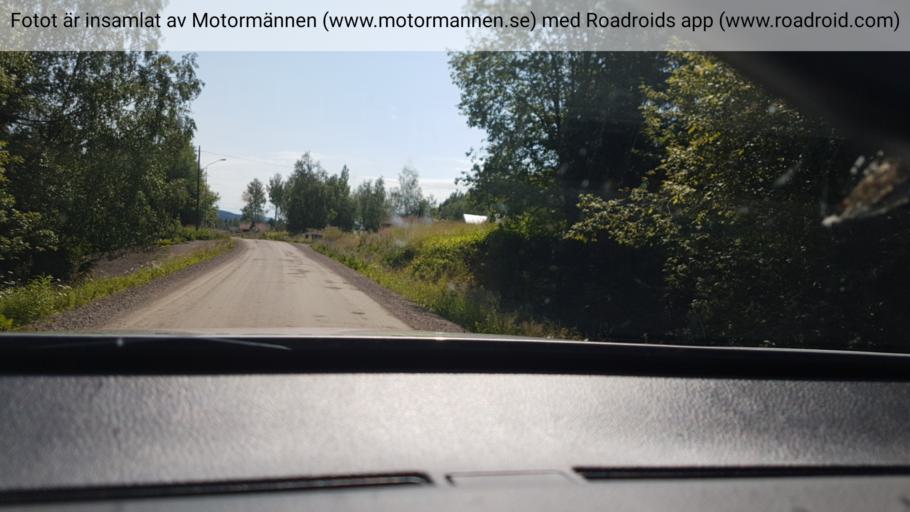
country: SE
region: Vaermland
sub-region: Torsby Kommun
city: Torsby
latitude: 60.5944
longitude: 13.0528
